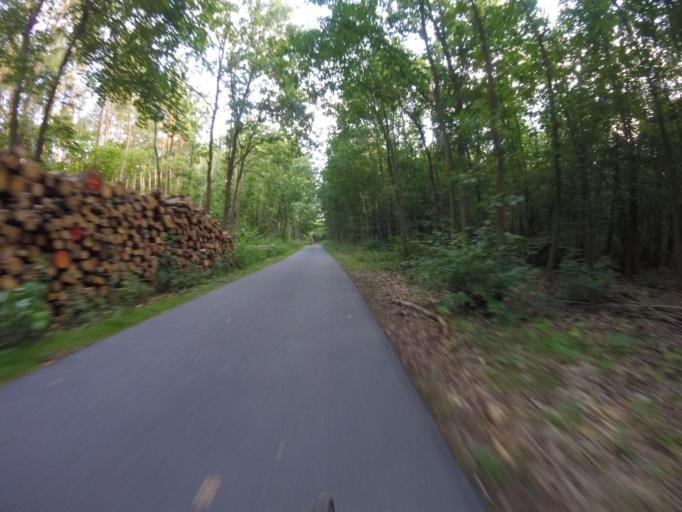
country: DE
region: Brandenburg
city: Petershagen
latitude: 52.5568
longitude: 13.8178
